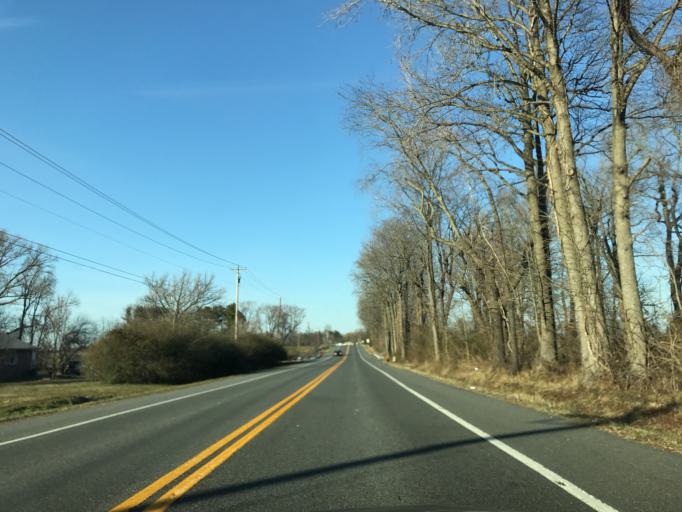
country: US
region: Maryland
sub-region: Queen Anne's County
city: Kingstown
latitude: 39.1737
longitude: -75.8589
